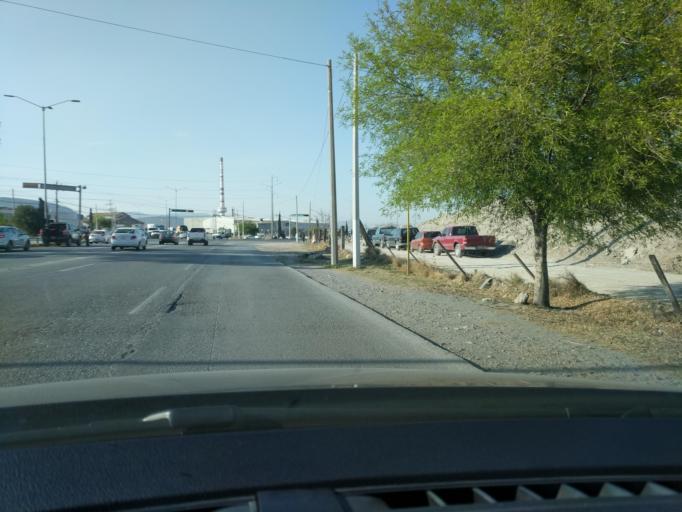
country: MX
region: Coahuila
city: Saltillo
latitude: 25.4778
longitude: -100.9837
